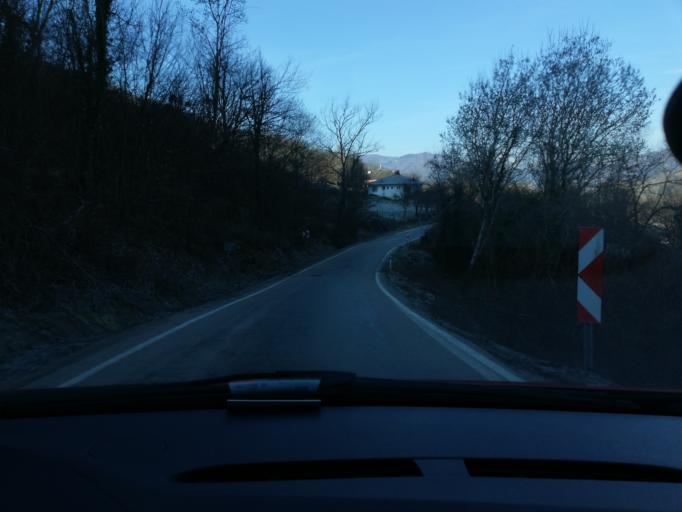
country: TR
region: Bartin
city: Kumluca
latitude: 41.4543
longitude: 32.5017
